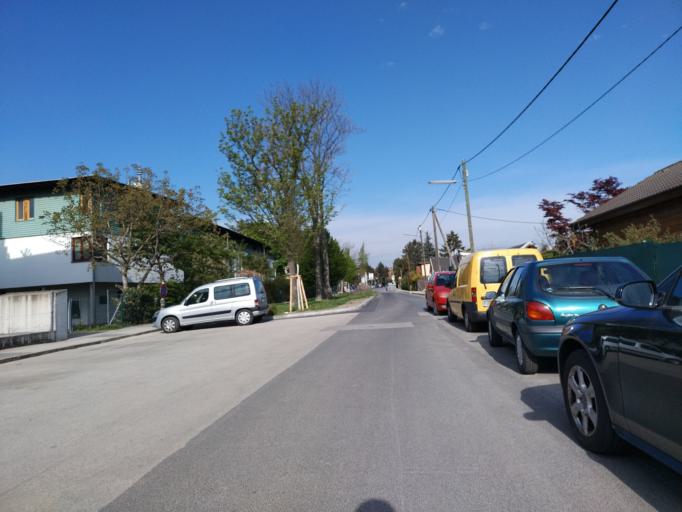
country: AT
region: Lower Austria
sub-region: Politischer Bezirk Modling
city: Vosendorf
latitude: 48.1585
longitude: 16.3145
